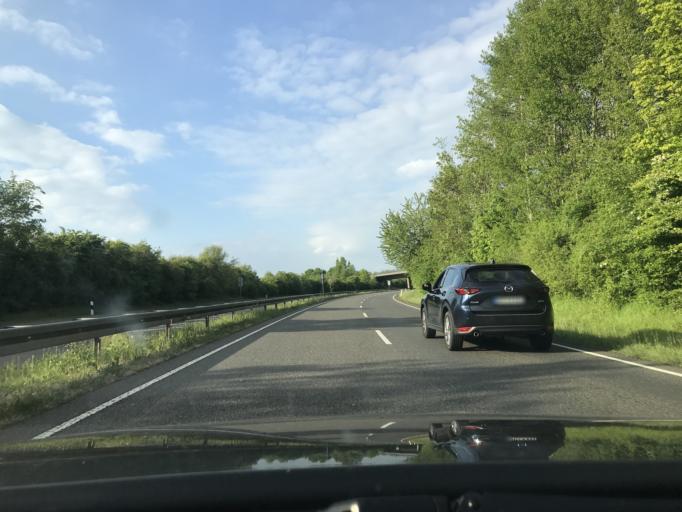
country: DE
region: North Rhine-Westphalia
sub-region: Regierungsbezirk Koln
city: Erftstadt
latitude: 50.8161
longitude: 6.8071
